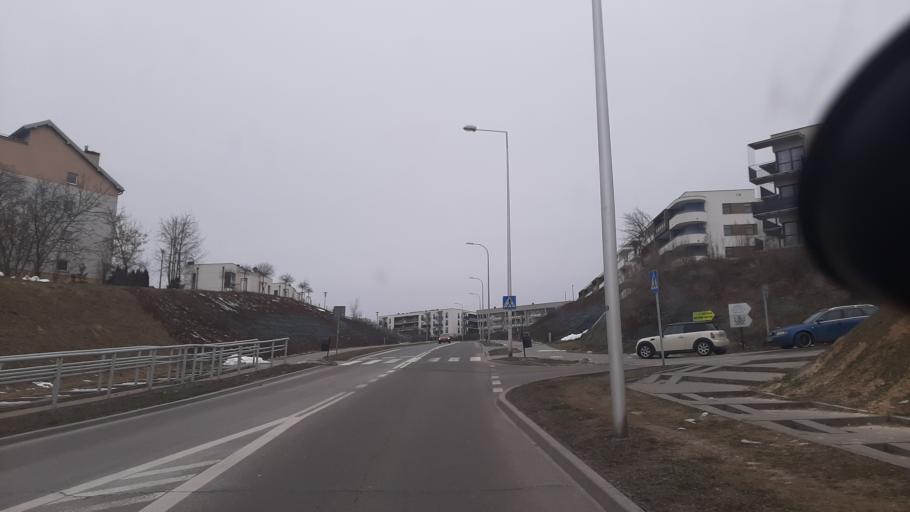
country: PL
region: Lublin Voivodeship
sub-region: Powiat lubelski
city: Lublin
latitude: 51.2706
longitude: 22.5825
